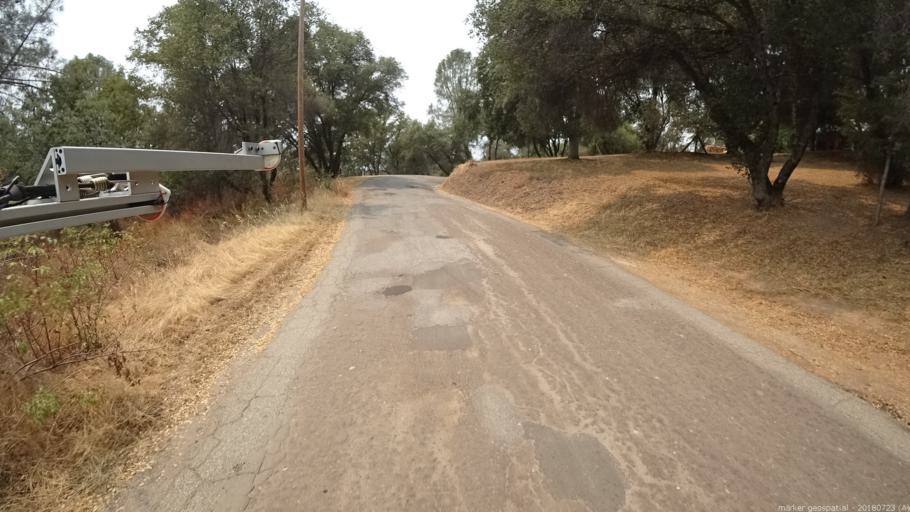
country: US
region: California
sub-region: Madera County
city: Oakhurst
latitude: 37.3411
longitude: -119.6537
